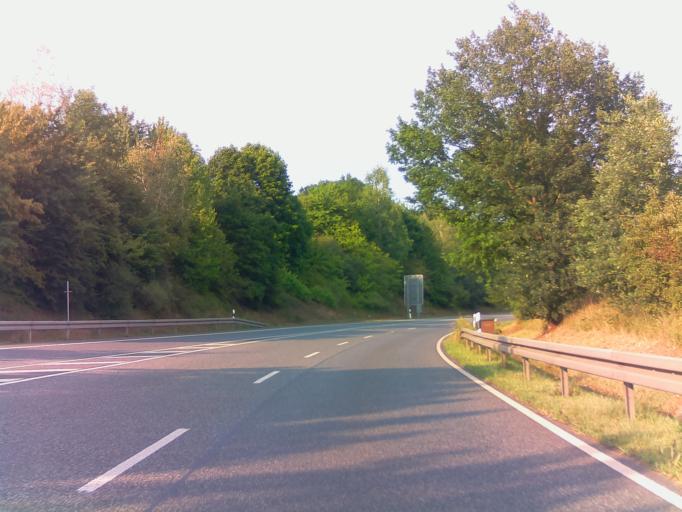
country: DE
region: Hesse
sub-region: Regierungsbezirk Kassel
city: Bad Hersfeld
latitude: 50.8663
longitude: 9.7306
